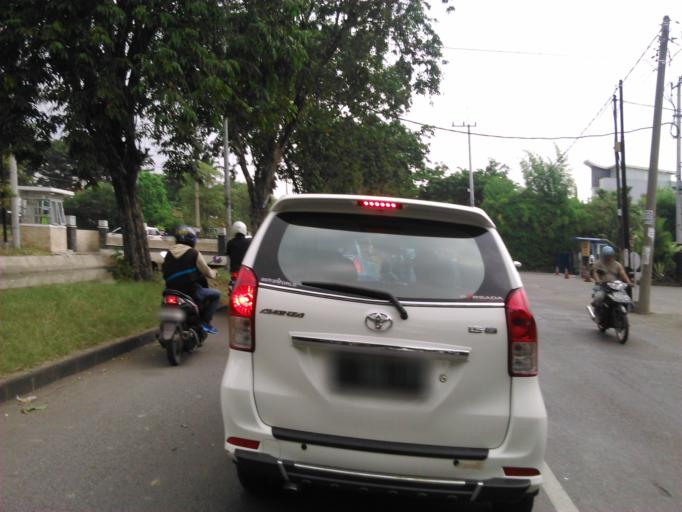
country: ID
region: East Java
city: Semampir
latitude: -7.2904
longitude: 112.7893
